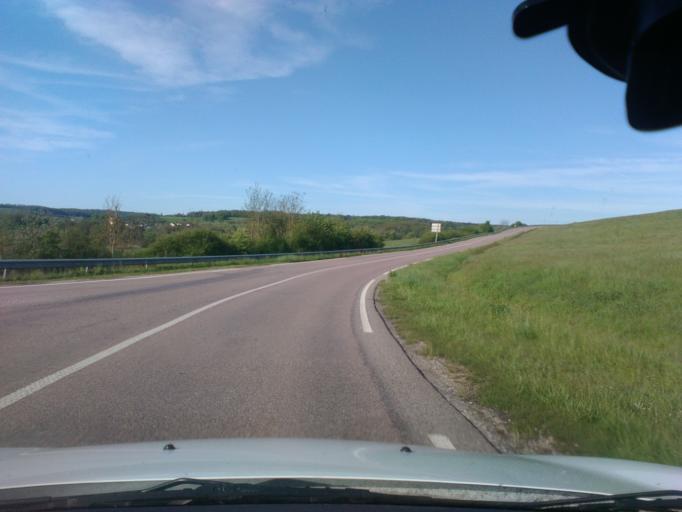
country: FR
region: Lorraine
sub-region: Departement des Vosges
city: Mirecourt
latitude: 48.2764
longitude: 6.1478
